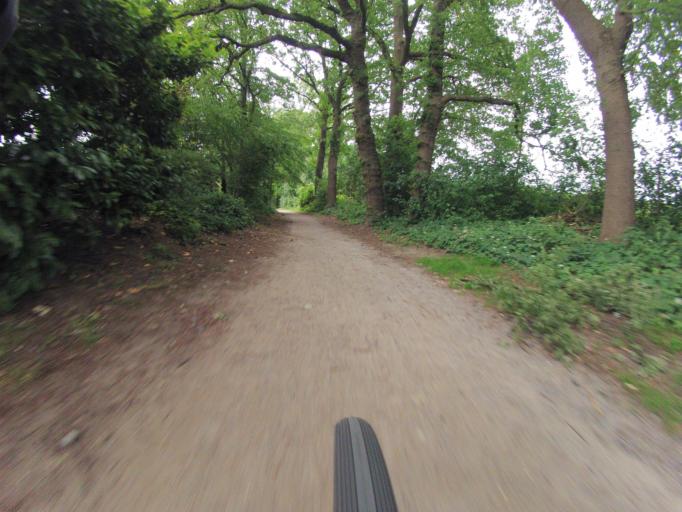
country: DE
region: North Rhine-Westphalia
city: Emsdetten
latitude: 52.1725
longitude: 7.5522
